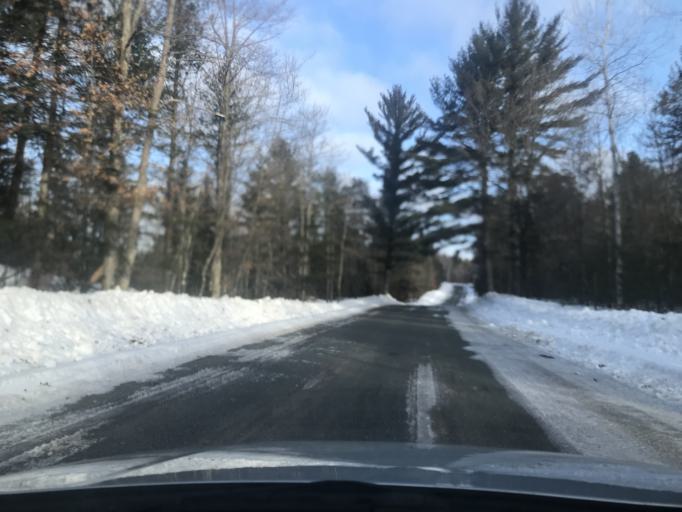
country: US
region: Wisconsin
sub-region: Marinette County
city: Niagara
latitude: 45.6288
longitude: -87.9676
